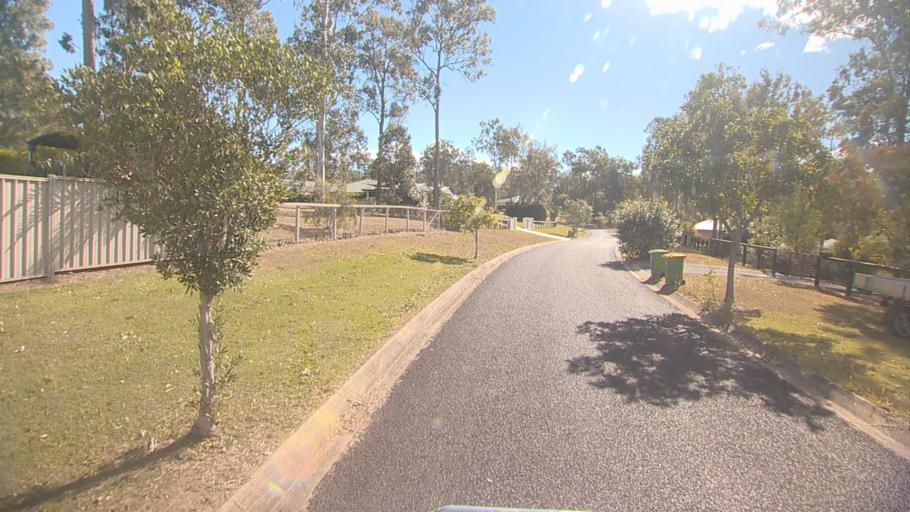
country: AU
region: Queensland
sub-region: Logan
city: North Maclean
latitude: -27.7487
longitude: 152.9384
